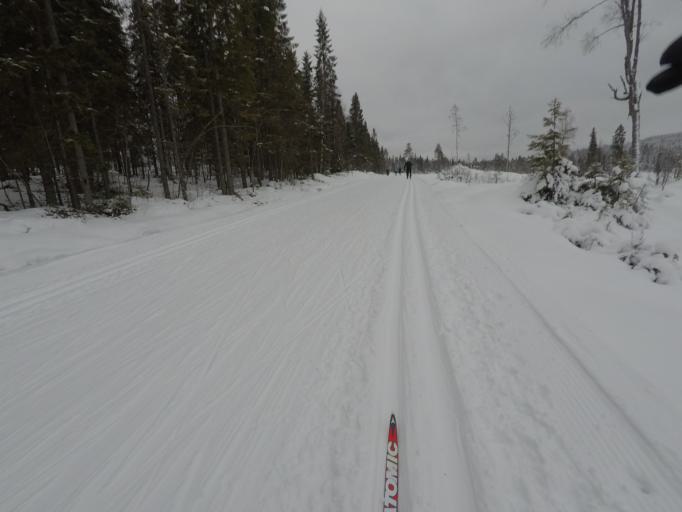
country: SE
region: Dalarna
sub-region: Ludvika Kommun
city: Abborrberget
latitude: 60.1509
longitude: 14.4894
